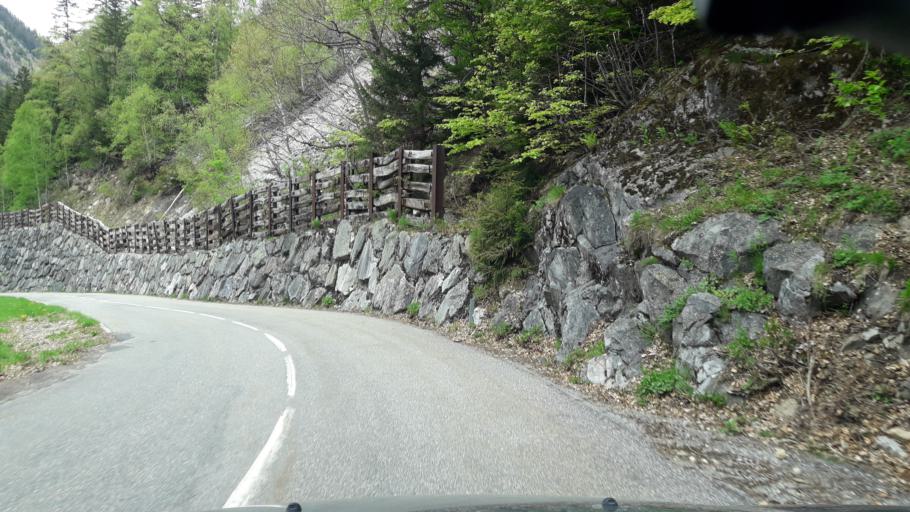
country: FR
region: Rhone-Alpes
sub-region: Departement de l'Isere
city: Huez
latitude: 45.2012
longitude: 6.0834
